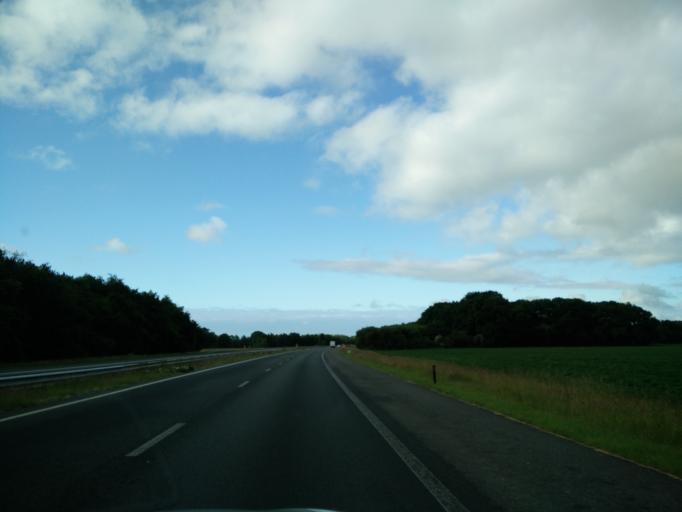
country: NL
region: Drenthe
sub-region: Gemeente Tynaarlo
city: Tynaarlo
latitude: 53.1006
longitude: 6.6122
